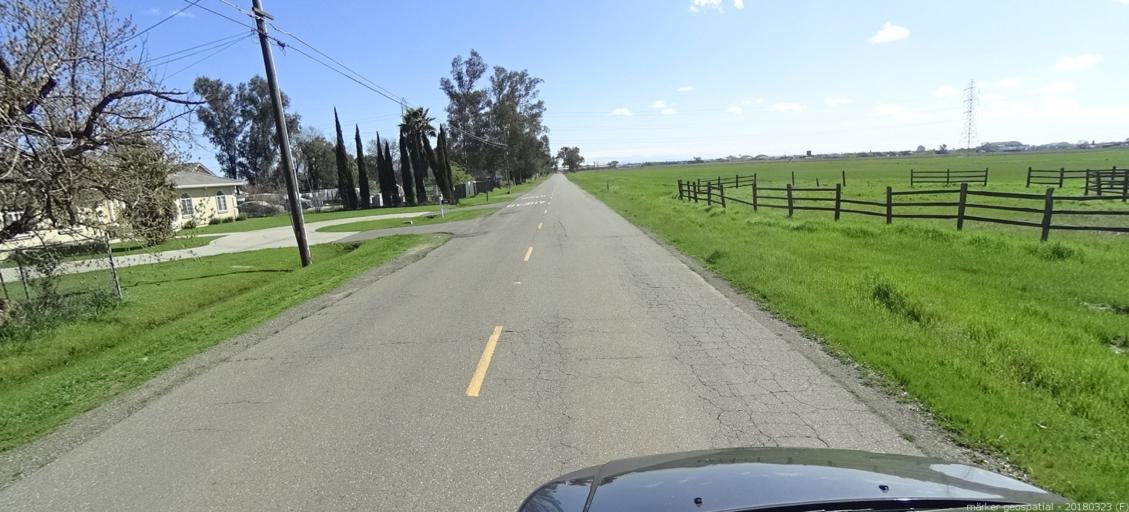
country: US
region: California
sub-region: Sacramento County
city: Rio Linda
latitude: 38.6691
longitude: -121.4280
